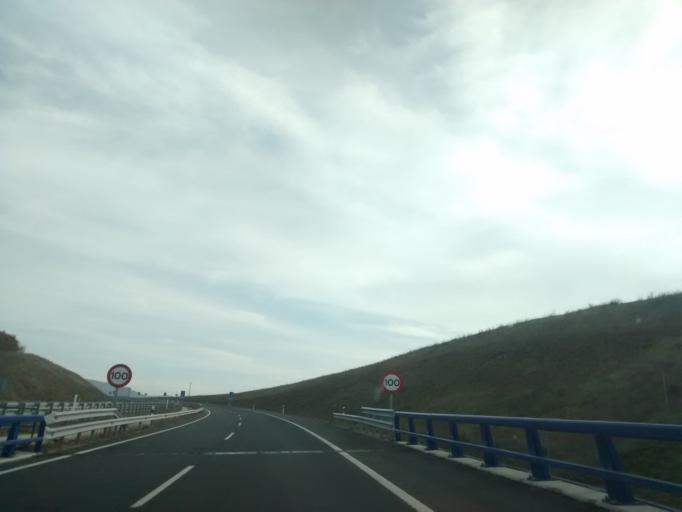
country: ES
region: Aragon
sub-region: Provincia de Zaragoza
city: Mianos
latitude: 42.6106
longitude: -0.9221
